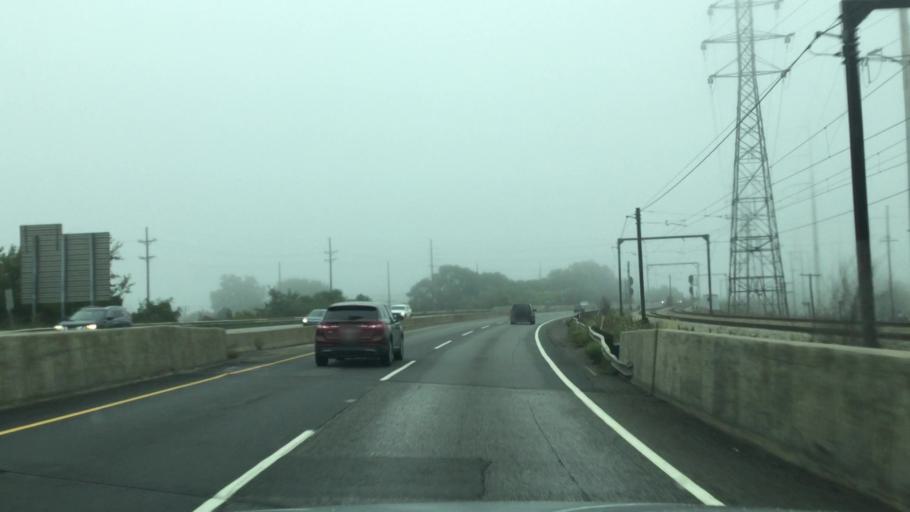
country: US
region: Illinois
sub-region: Cook County
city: Calumet City
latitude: 41.6249
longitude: -87.4921
